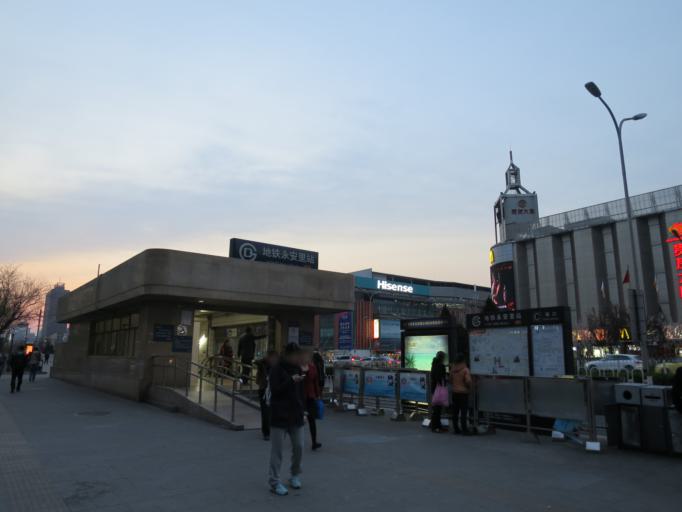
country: CN
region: Beijing
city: Chaowai
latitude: 39.9066
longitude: 116.4452
